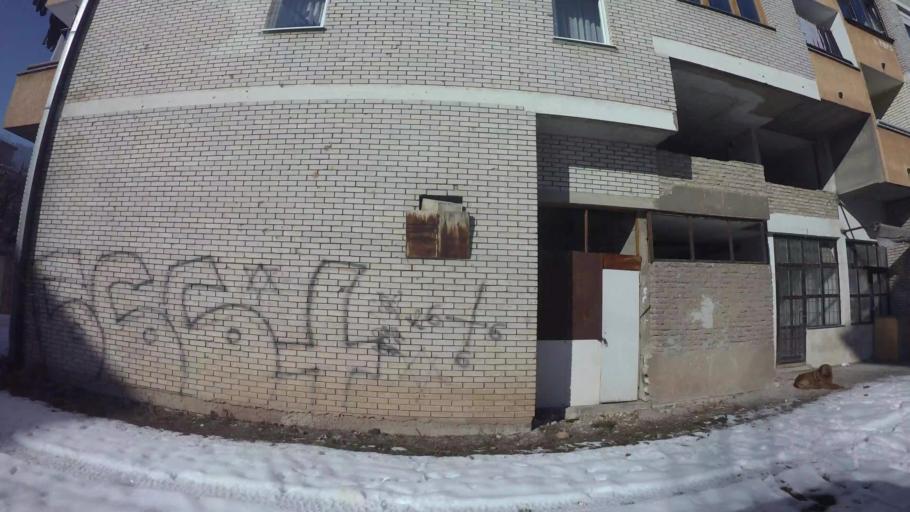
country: BA
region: Federation of Bosnia and Herzegovina
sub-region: Kanton Sarajevo
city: Sarajevo
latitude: 43.8002
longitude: 18.3101
